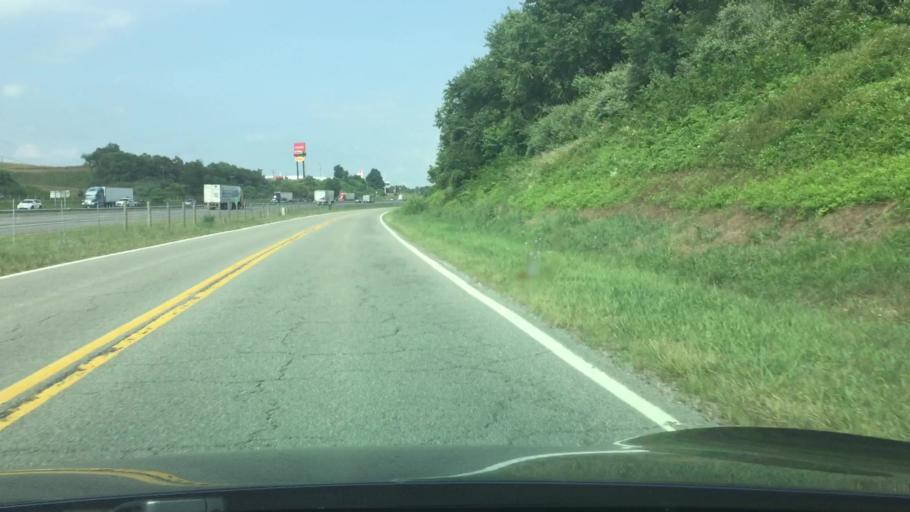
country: US
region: Virginia
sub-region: Wythe County
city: Wytheville
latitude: 36.9379
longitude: -80.9868
